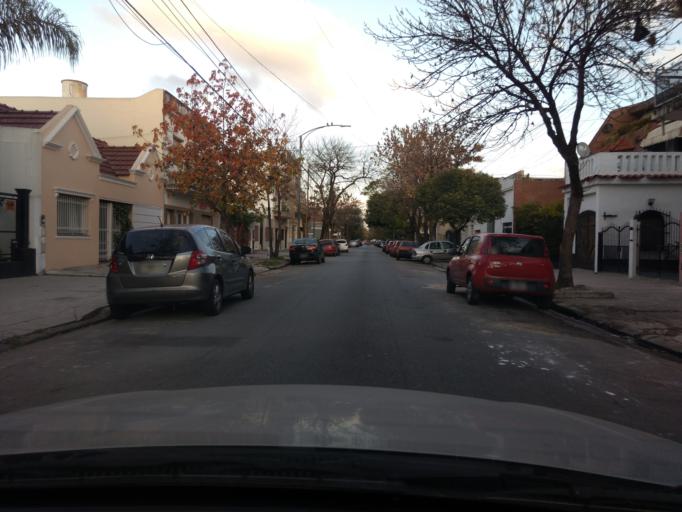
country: AR
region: Buenos Aires F.D.
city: Villa Santa Rita
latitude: -34.6110
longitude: -58.5149
